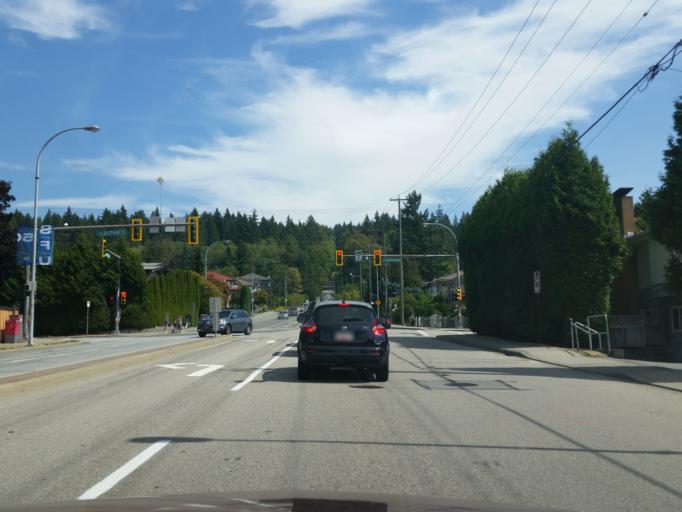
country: CA
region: British Columbia
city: Burnaby
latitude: 49.2804
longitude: -122.9542
